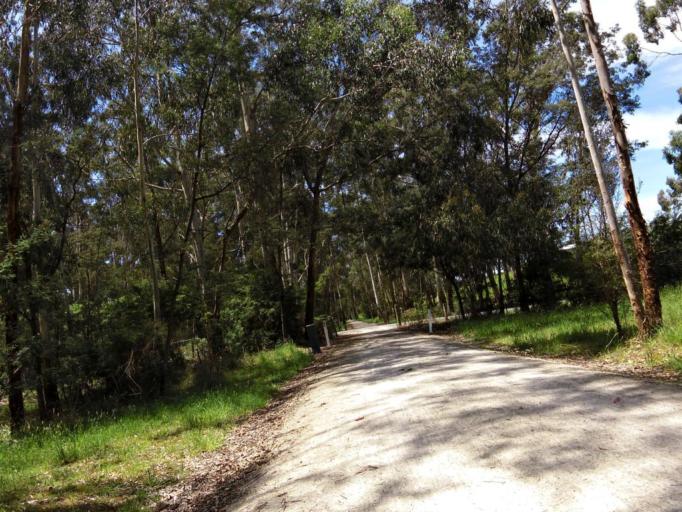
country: AU
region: Victoria
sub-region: Yarra Ranges
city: Woori Yallock
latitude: -37.7581
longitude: 145.4758
